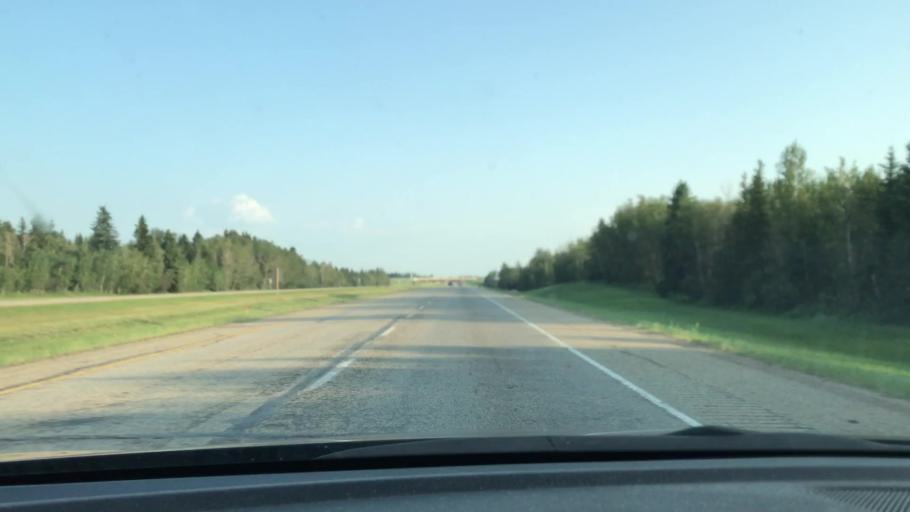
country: CA
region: Alberta
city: Lacombe
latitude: 52.5690
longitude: -113.6631
